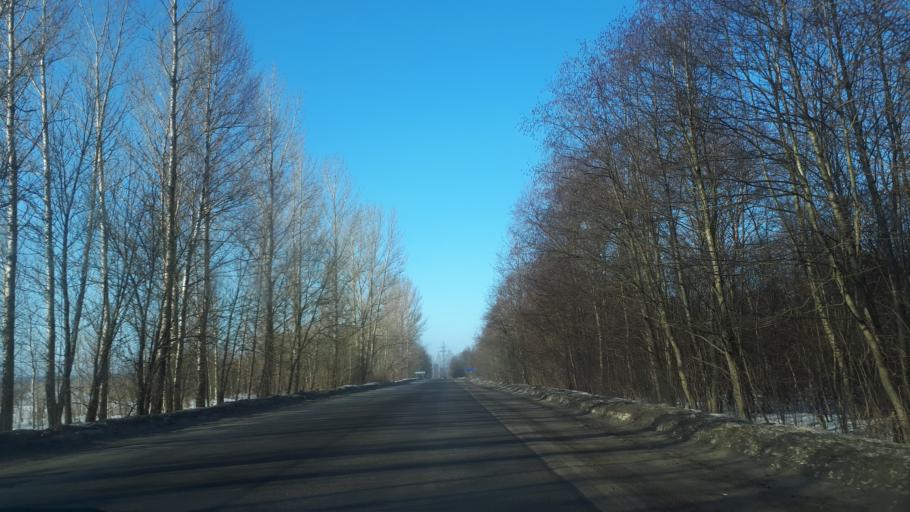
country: RU
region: Jaroslavl
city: Konstantinovskiy
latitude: 57.8178
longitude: 39.5749
